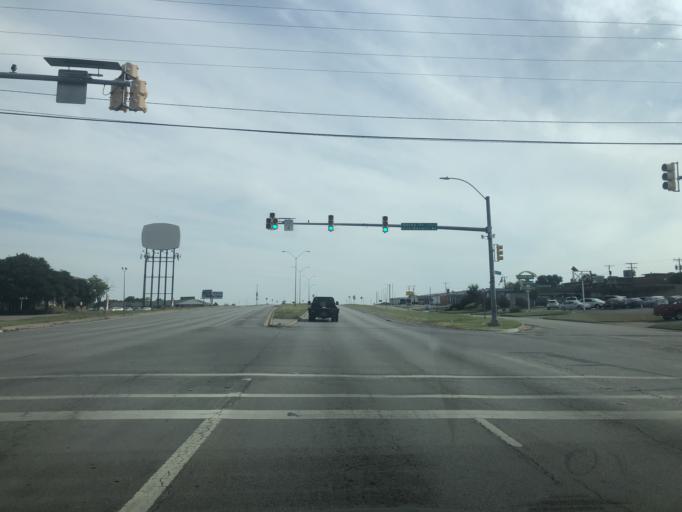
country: US
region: Texas
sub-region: Tarrant County
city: Benbrook
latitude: 32.7123
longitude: -97.4459
